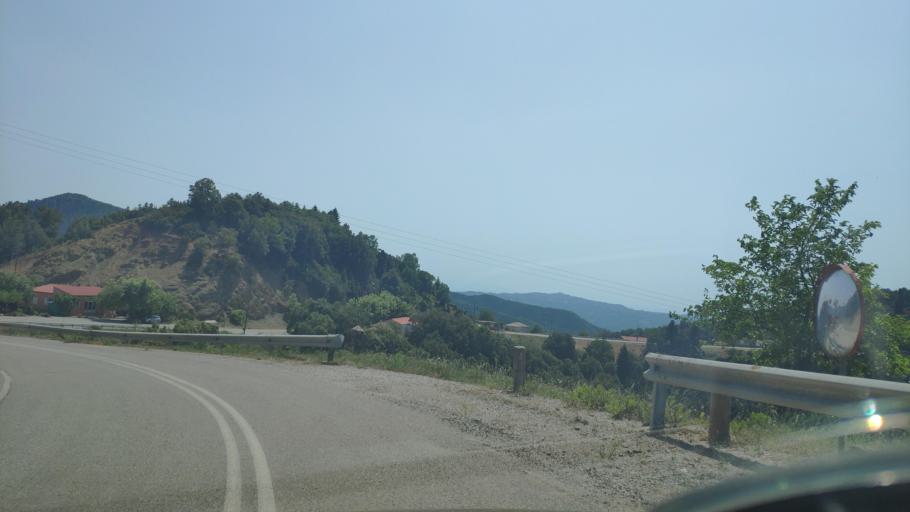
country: GR
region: Epirus
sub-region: Nomos Artas
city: Ano Kalentini
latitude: 39.2361
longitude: 21.2268
